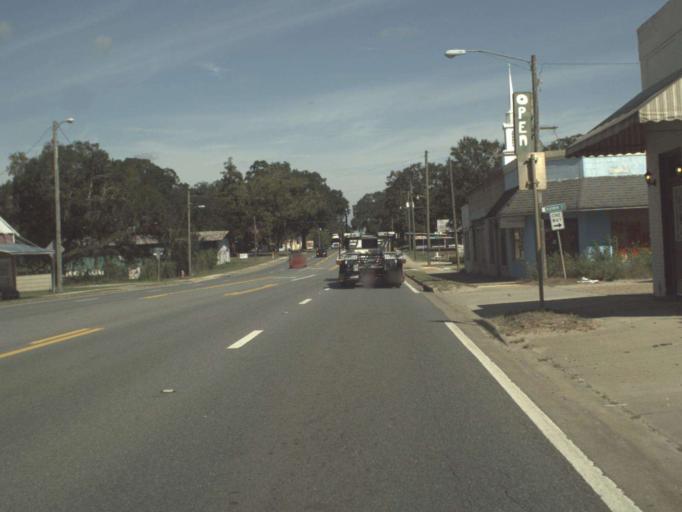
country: US
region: Florida
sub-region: Jackson County
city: Marianna
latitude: 30.7962
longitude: -85.3766
